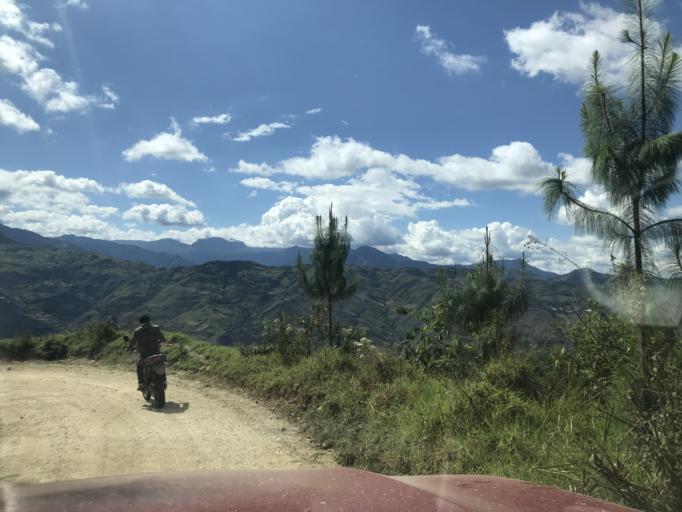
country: PE
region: Cajamarca
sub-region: Provincia de Chota
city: Querocoto
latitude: -6.3331
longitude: -79.0713
